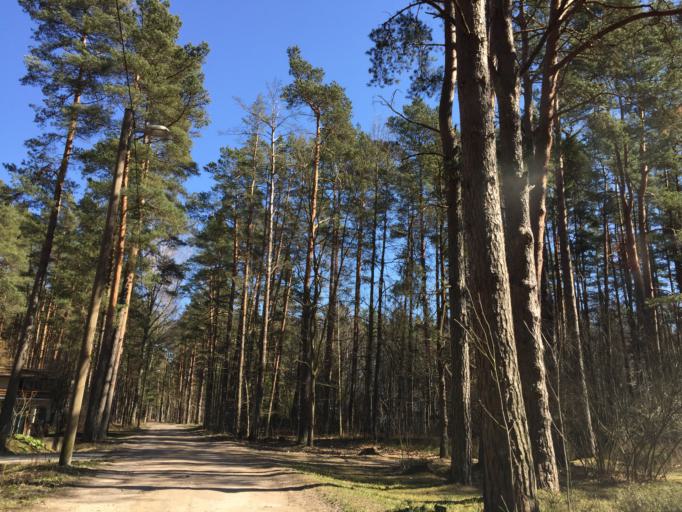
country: LV
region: Jurmala
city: Jurmala
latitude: 56.9492
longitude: 23.6782
